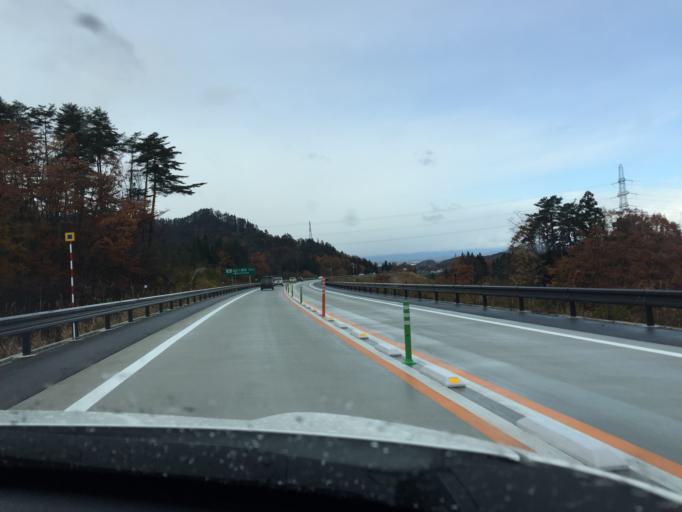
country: JP
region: Yamagata
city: Yonezawa
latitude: 37.8834
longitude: 140.1756
